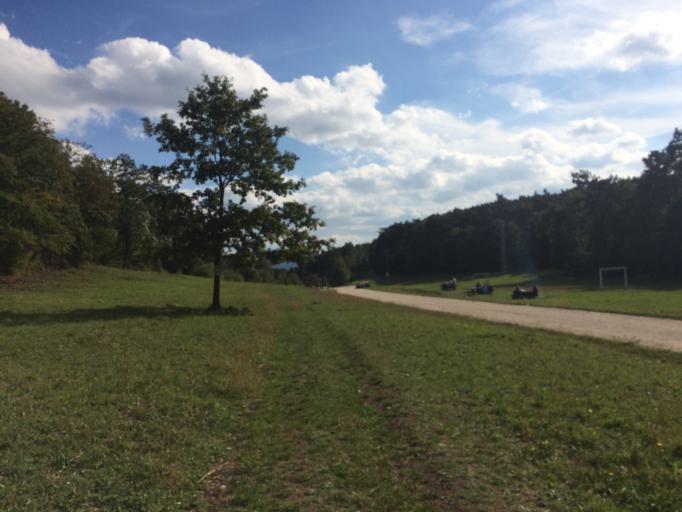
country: HU
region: Pest
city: Nagymaros
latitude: 47.7995
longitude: 18.9434
